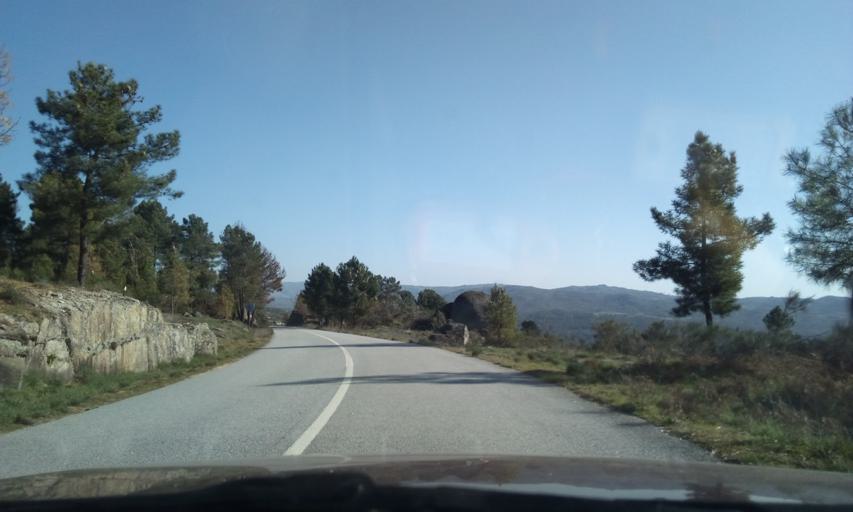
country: PT
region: Guarda
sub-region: Fornos de Algodres
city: Fornos de Algodres
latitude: 40.6363
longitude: -7.4813
